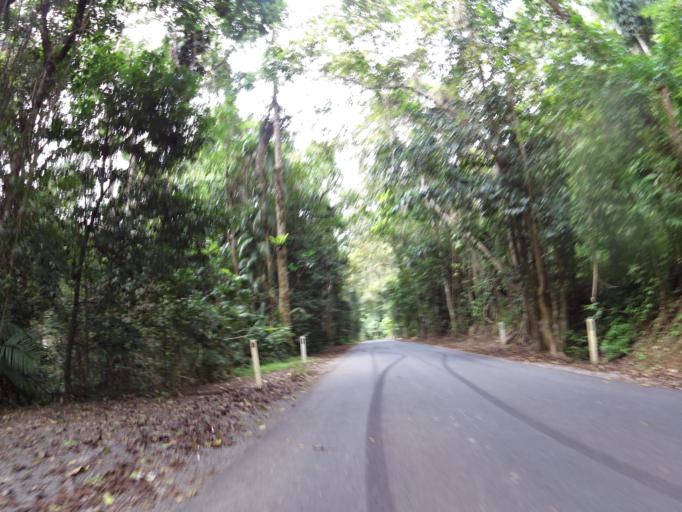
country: AU
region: Queensland
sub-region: Cairns
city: Woree
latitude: -16.9613
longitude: 145.6807
